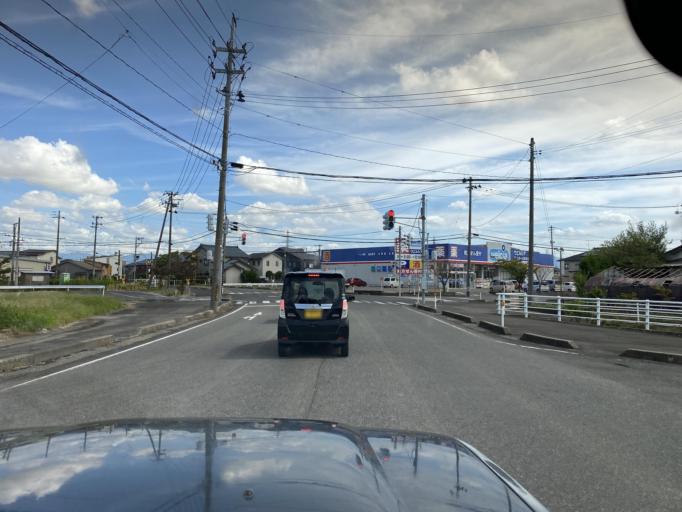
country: JP
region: Niigata
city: Niitsu-honcho
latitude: 37.8144
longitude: 139.1156
